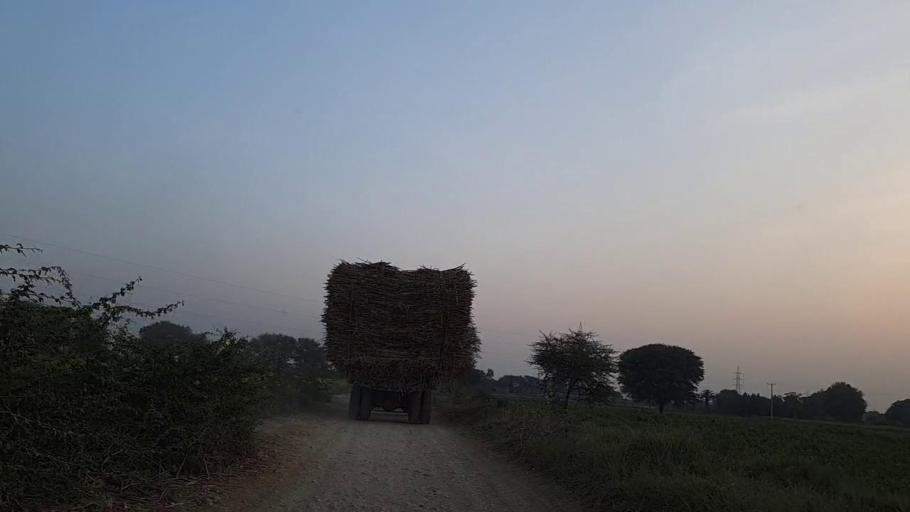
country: PK
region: Sindh
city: Tando Ghulam Ali
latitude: 25.1482
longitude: 68.9408
